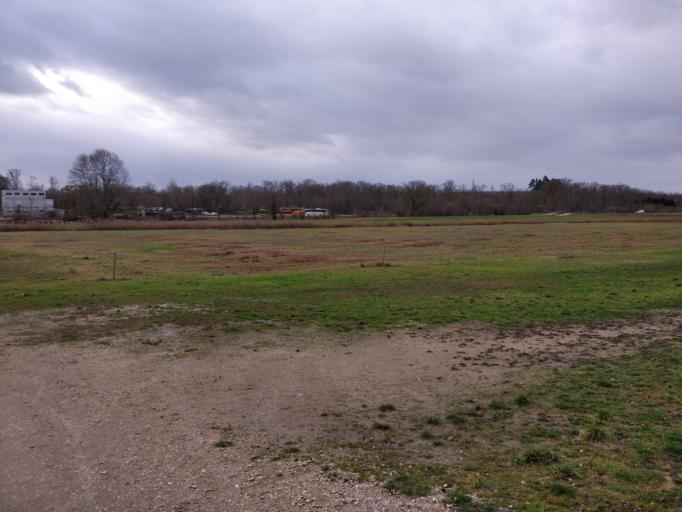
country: FR
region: Centre
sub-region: Departement du Loir-et-Cher
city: Saint-Dye-sur-Loire
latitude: 47.6182
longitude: 1.5120
